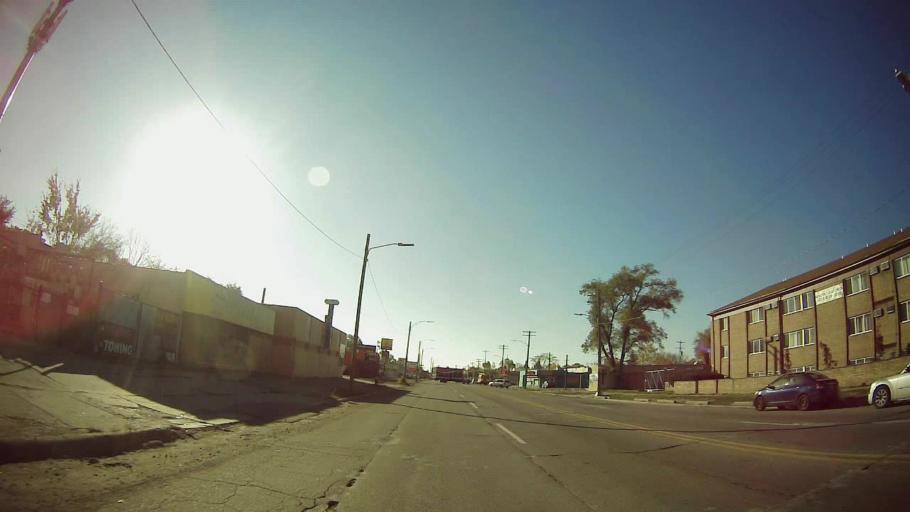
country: US
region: Michigan
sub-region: Wayne County
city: Dearborn
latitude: 42.3668
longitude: -83.1972
